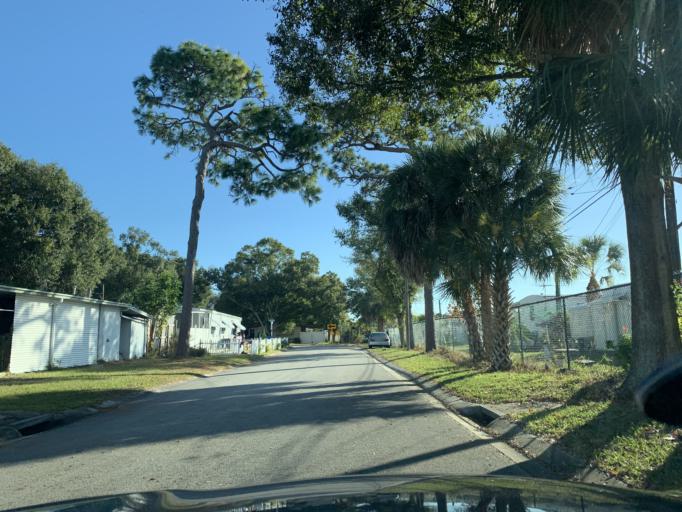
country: US
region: Florida
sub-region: Pinellas County
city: Kenneth City
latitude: 27.8173
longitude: -82.7441
